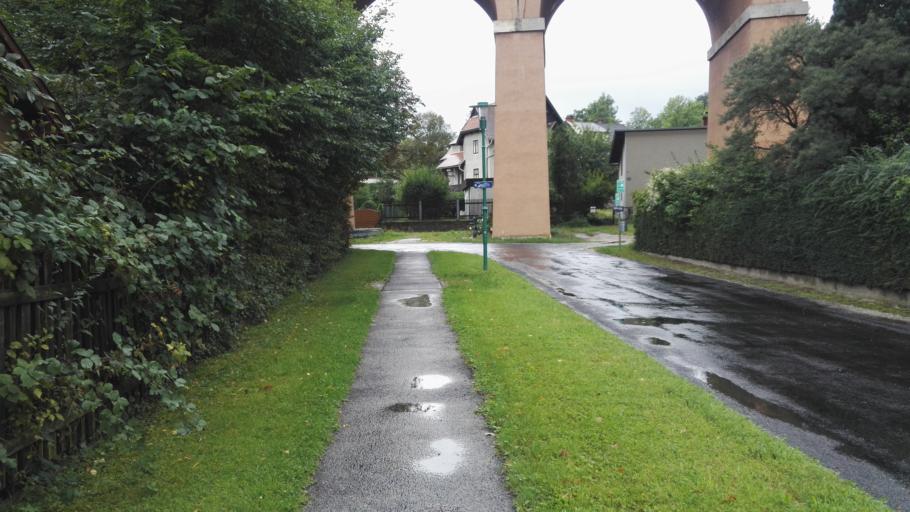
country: AT
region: Lower Austria
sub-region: Politischer Bezirk Neunkirchen
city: Payerbach
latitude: 47.6928
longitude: 15.8571
